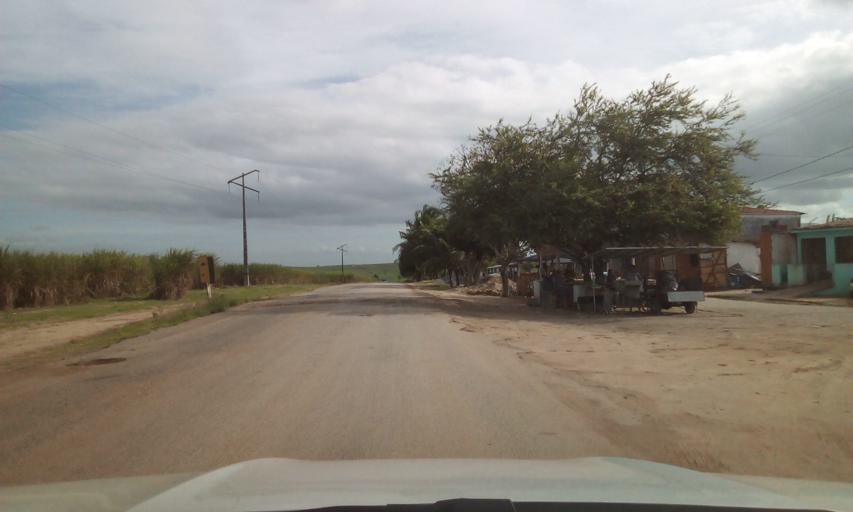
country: BR
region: Paraiba
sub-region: Santa Rita
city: Santa Rita
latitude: -6.9785
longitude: -34.9837
